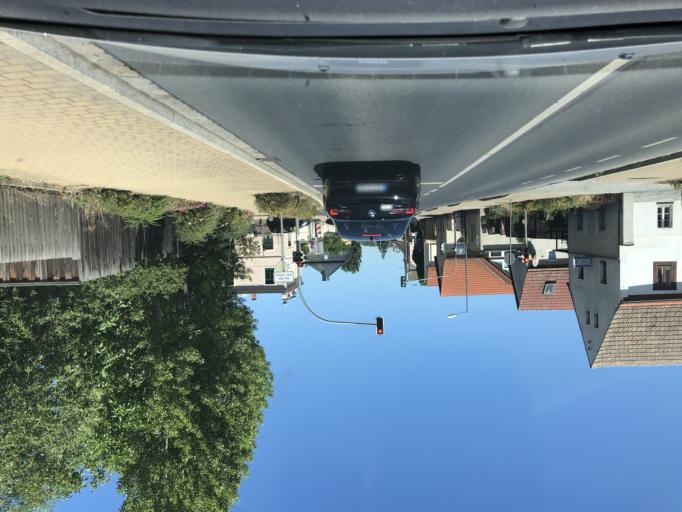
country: DE
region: Saxony
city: Coswig
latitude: 51.1180
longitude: 13.6024
